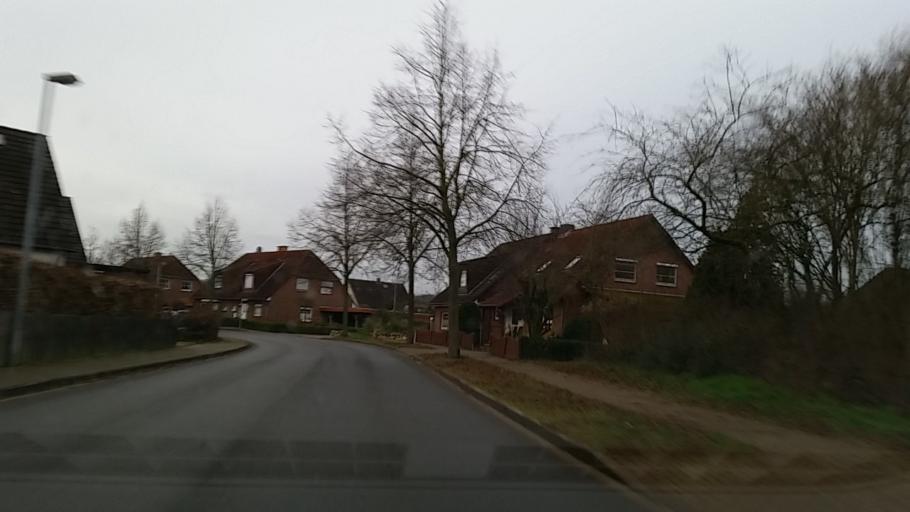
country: DE
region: Lower Saxony
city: Wolfsburg
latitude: 52.4257
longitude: 10.8416
